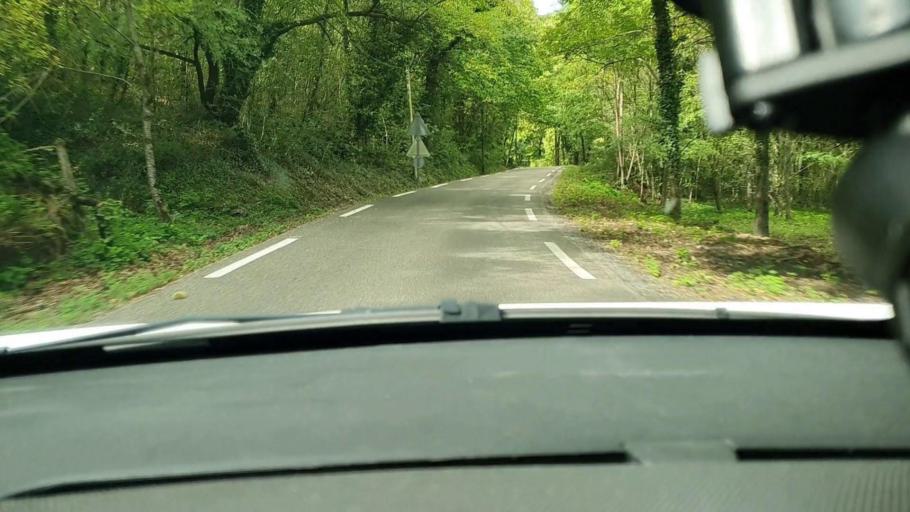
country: FR
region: Languedoc-Roussillon
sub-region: Departement du Gard
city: Besseges
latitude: 44.3040
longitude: 4.0124
